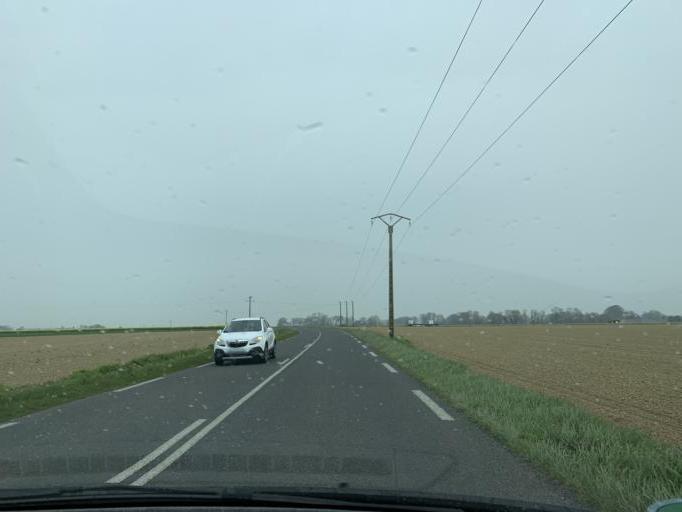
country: FR
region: Haute-Normandie
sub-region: Departement de la Seine-Maritime
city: Cany-Barville
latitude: 49.7934
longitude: 0.6614
